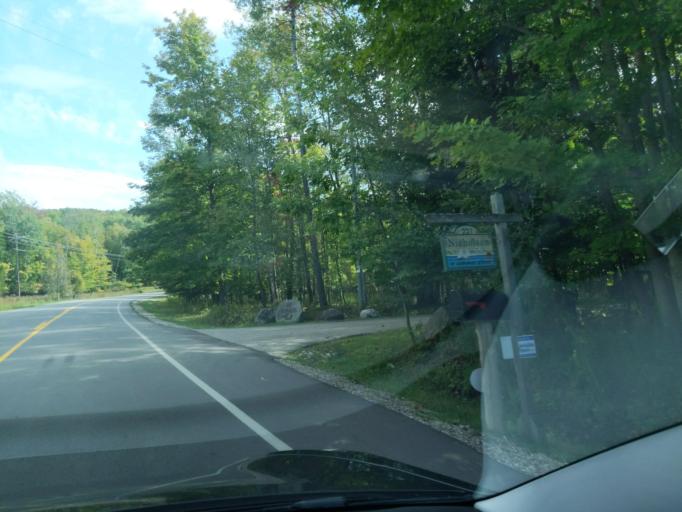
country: US
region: Michigan
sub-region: Antrim County
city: Bellaire
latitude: 45.0385
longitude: -85.2983
